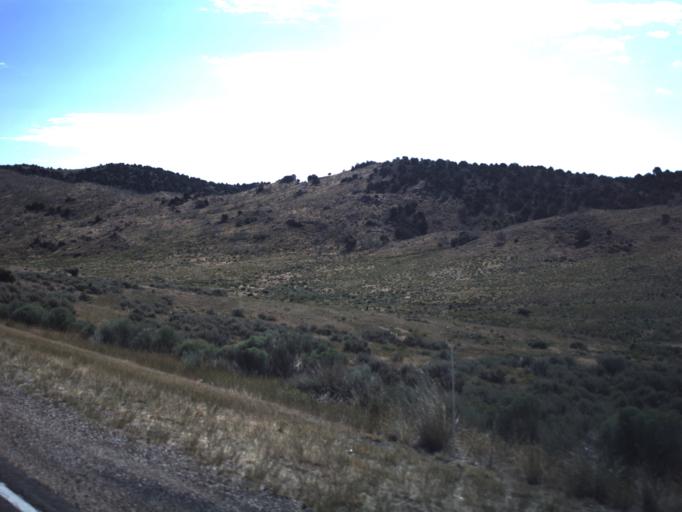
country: US
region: Utah
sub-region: Utah County
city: Genola
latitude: 39.9652
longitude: -112.0942
